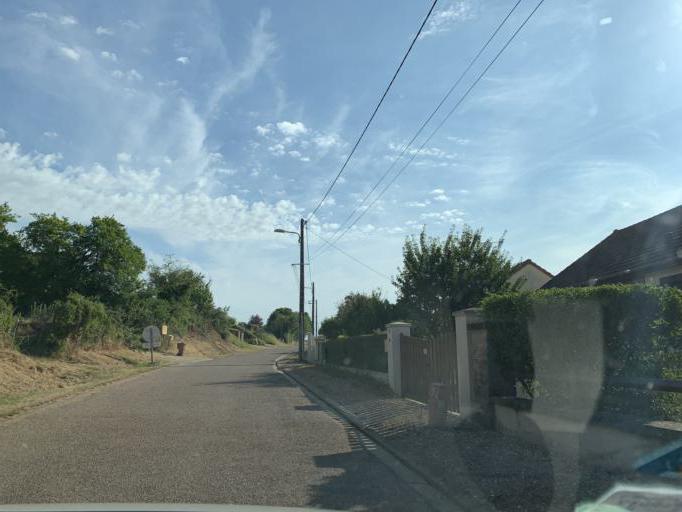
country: FR
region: Bourgogne
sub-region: Departement de la Nievre
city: Varzy
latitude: 47.4491
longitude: 3.4164
